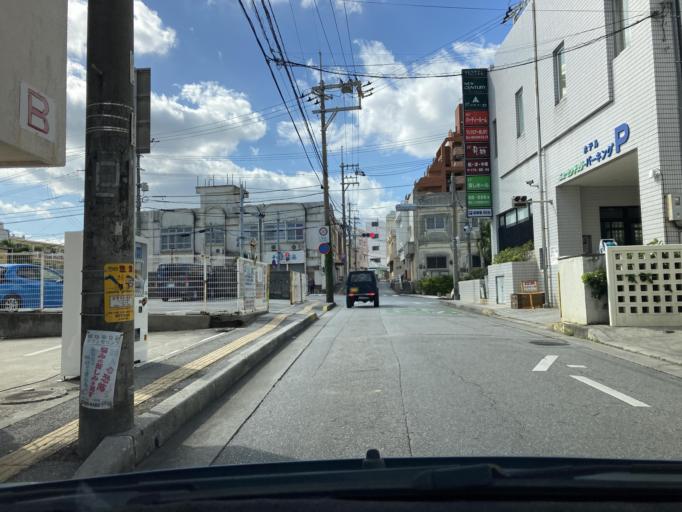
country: JP
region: Okinawa
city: Okinawa
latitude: 26.3325
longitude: 127.7988
